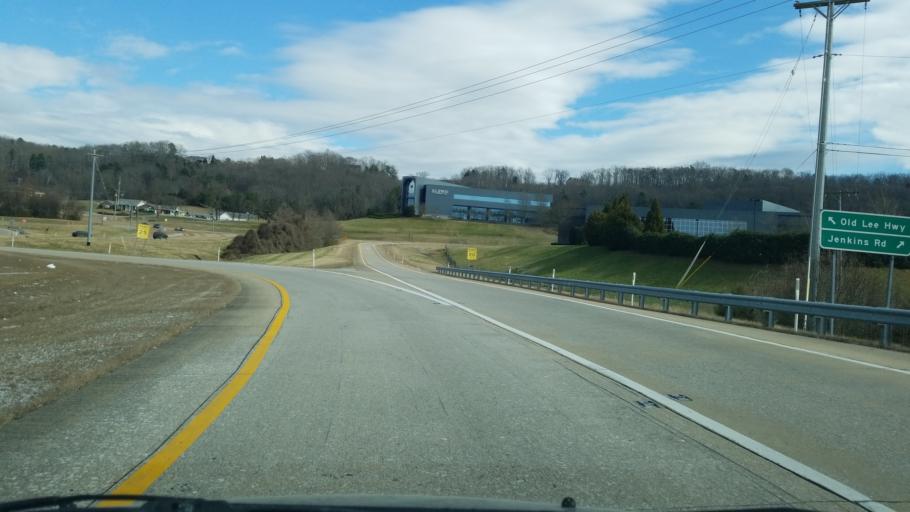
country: US
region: Tennessee
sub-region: Hamilton County
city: Harrison
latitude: 35.0576
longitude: -85.1305
